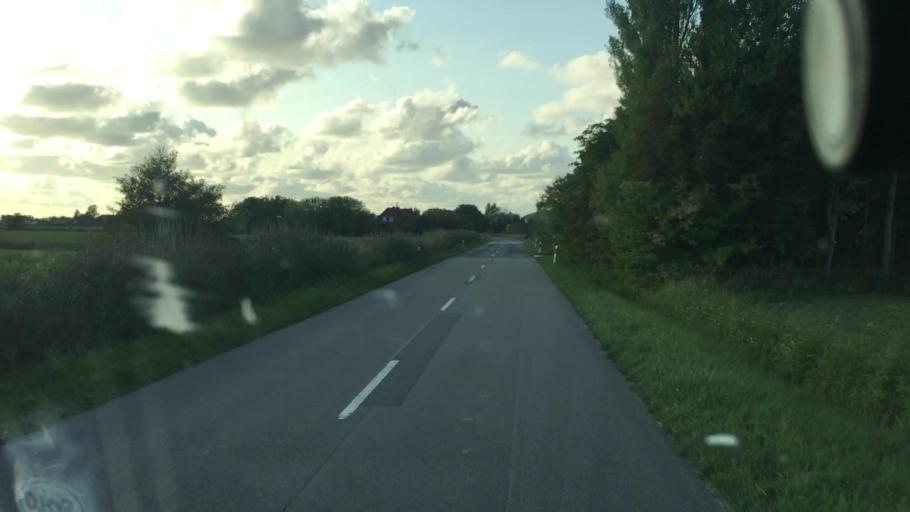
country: DE
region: Lower Saxony
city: Werdum
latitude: 53.6790
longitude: 7.7135
